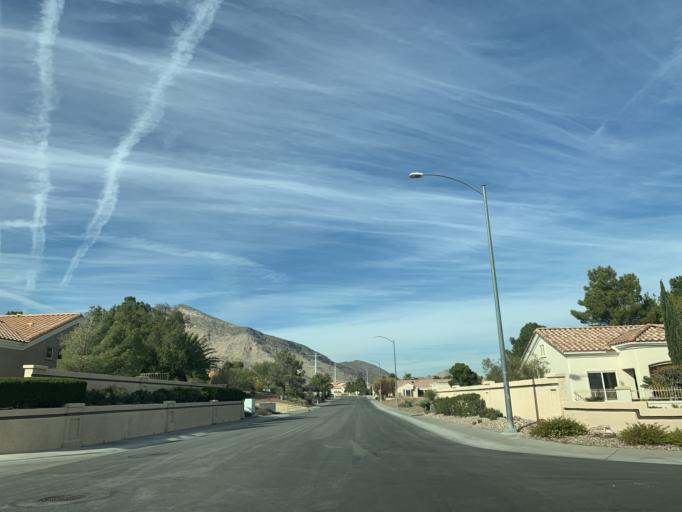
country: US
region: Nevada
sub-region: Clark County
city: Summerlin South
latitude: 36.2139
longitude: -115.3255
